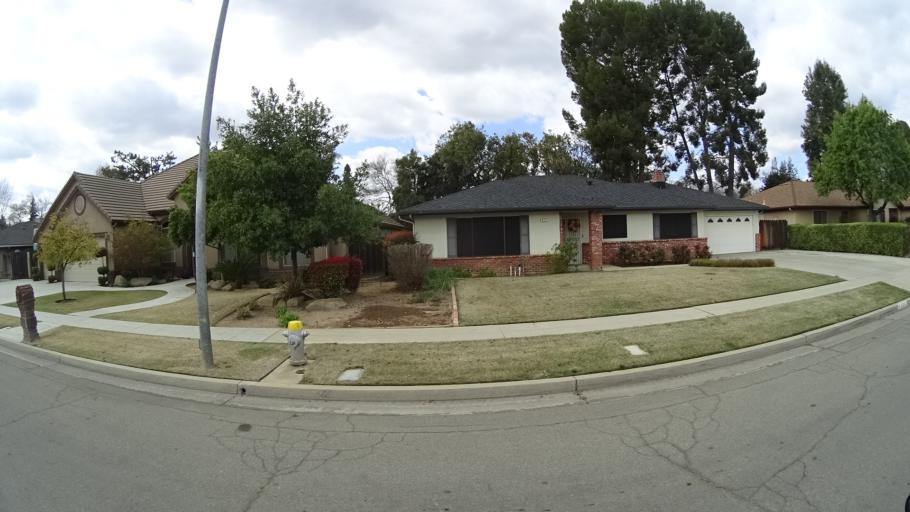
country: US
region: California
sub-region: Fresno County
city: Fresno
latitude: 36.8284
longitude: -119.8484
